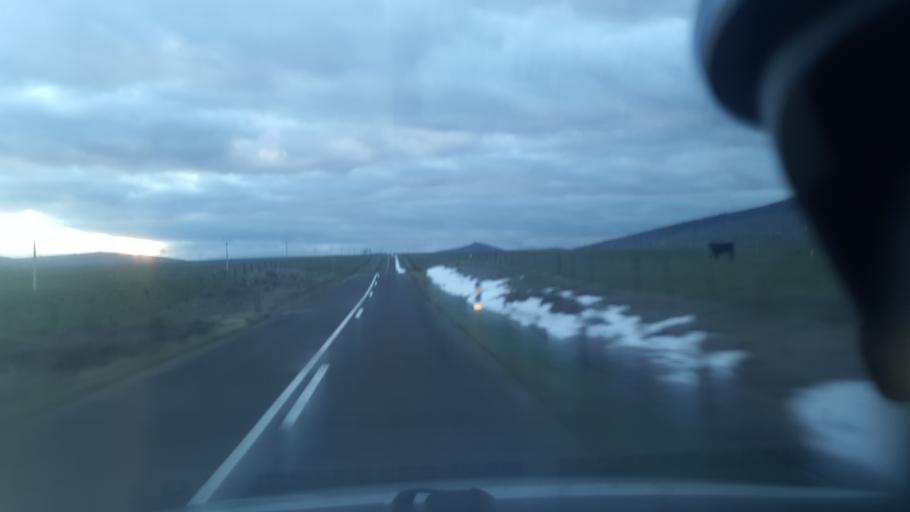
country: ES
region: Castille and Leon
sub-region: Provincia de Segovia
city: Villacastin
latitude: 40.6934
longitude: -4.4114
